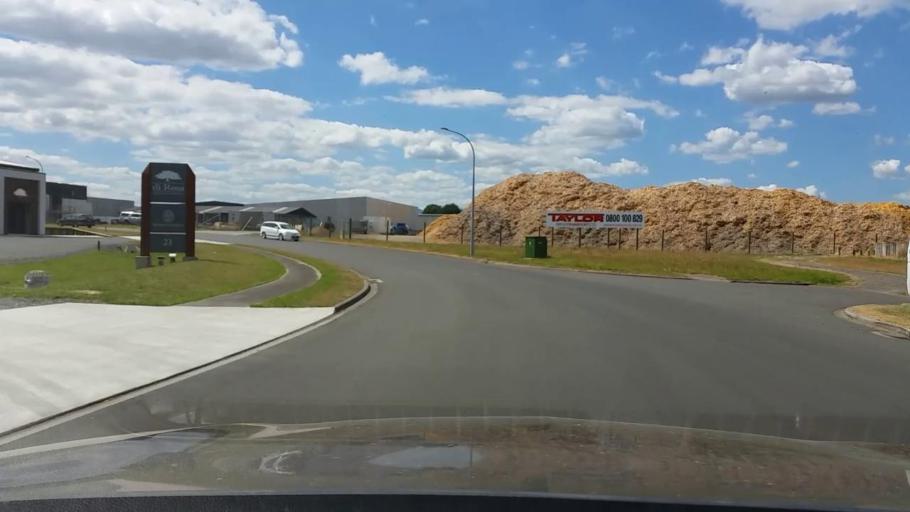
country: NZ
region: Waikato
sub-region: Matamata-Piako District
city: Matamata
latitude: -37.8178
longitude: 175.7963
